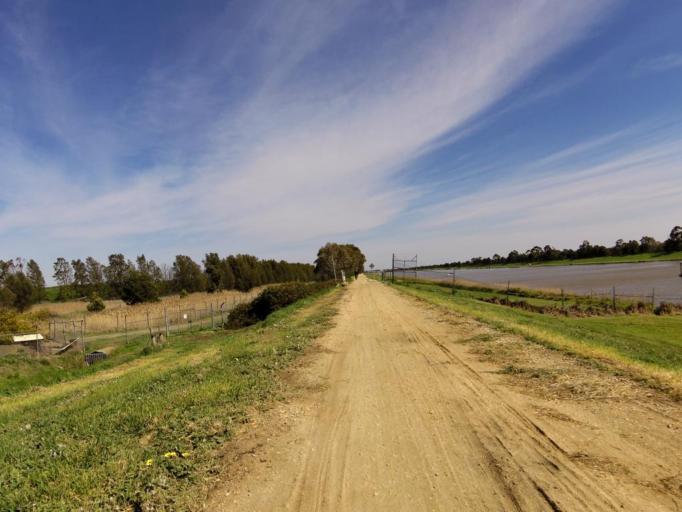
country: AU
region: Victoria
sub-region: Kingston
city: Patterson Lakes
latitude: -38.0470
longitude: 145.1715
